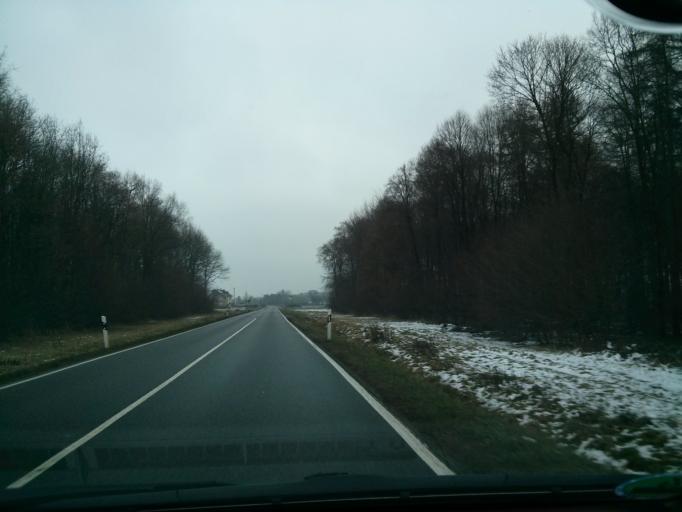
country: DE
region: North Rhine-Westphalia
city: Meckenheim
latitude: 50.6689
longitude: 7.0145
